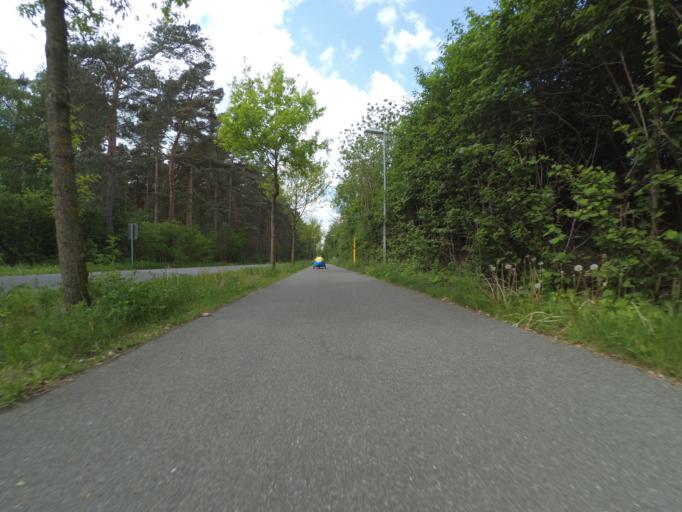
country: DE
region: Lower Saxony
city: Lachendorf
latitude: 52.6085
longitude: 10.2470
